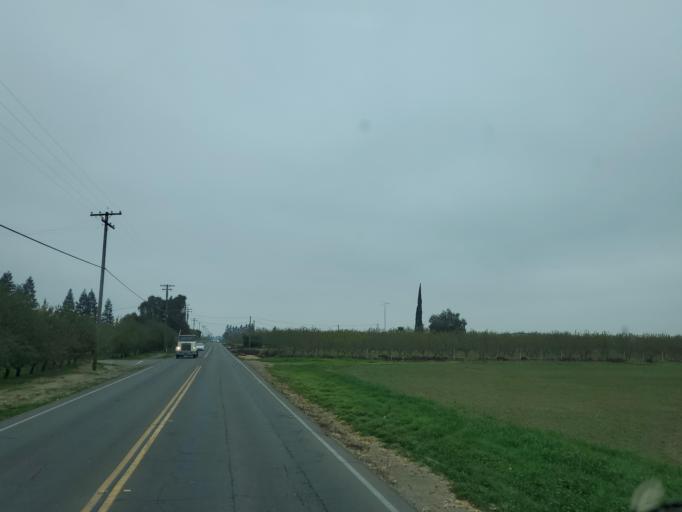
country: US
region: California
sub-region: Stanislaus County
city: Hughson
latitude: 37.5627
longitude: -120.8470
